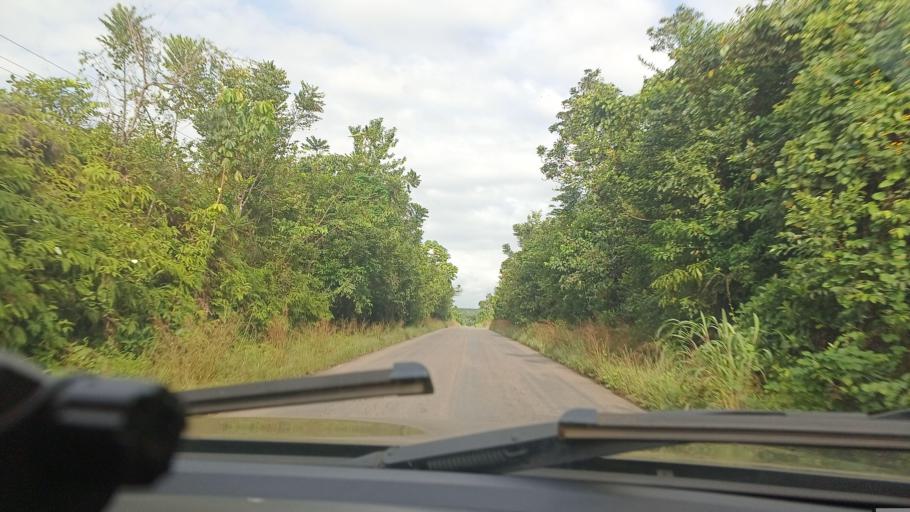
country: LR
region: Bomi
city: Tubmanburg
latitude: 6.7108
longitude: -10.9342
